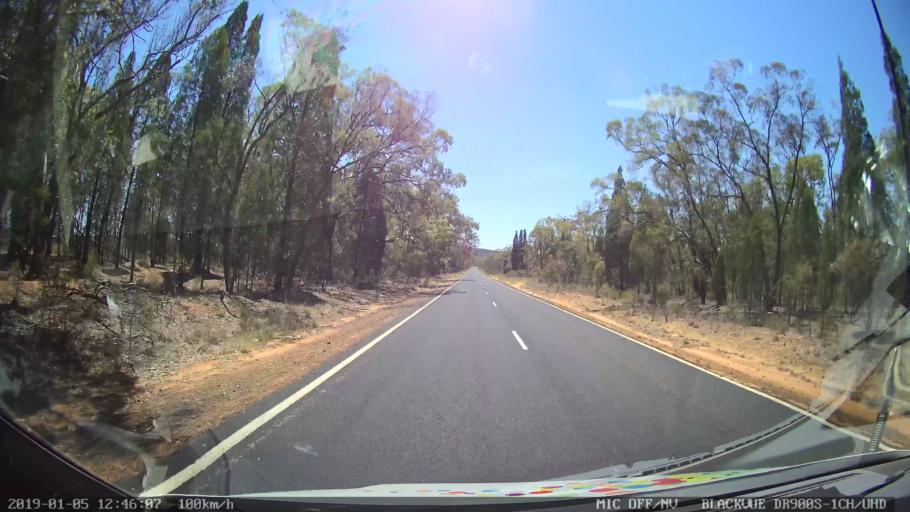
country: AU
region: New South Wales
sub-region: Warrumbungle Shire
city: Coonabarabran
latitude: -31.1212
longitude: 149.5585
